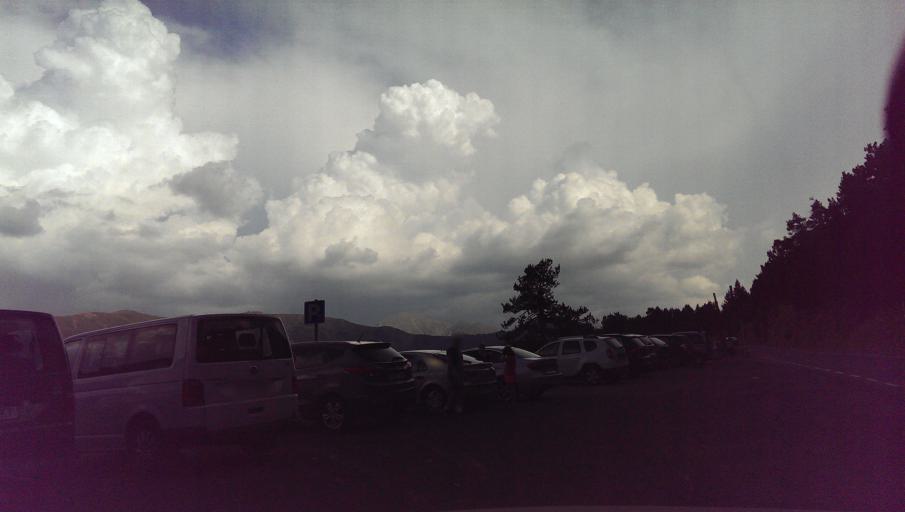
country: AD
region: Canillo
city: Canillo
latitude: 42.5710
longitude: 1.5870
